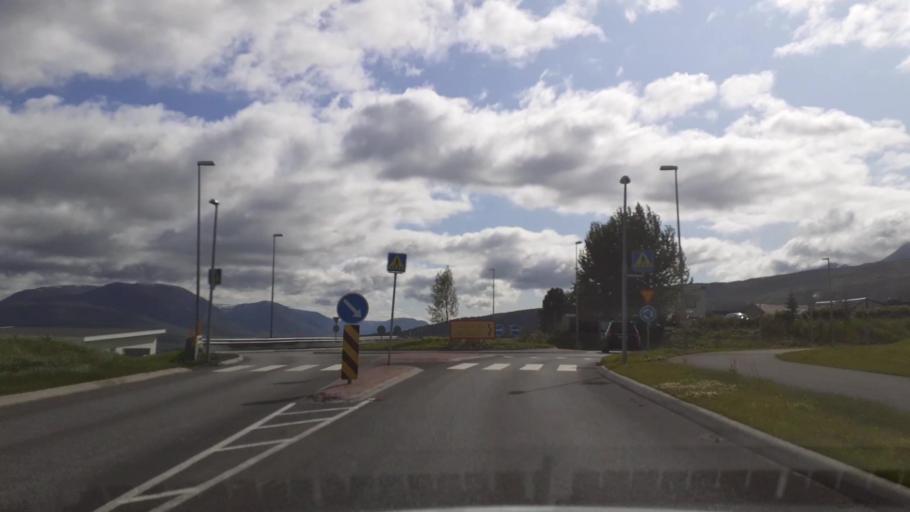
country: IS
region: Northeast
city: Akureyri
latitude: 65.6621
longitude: -18.0894
